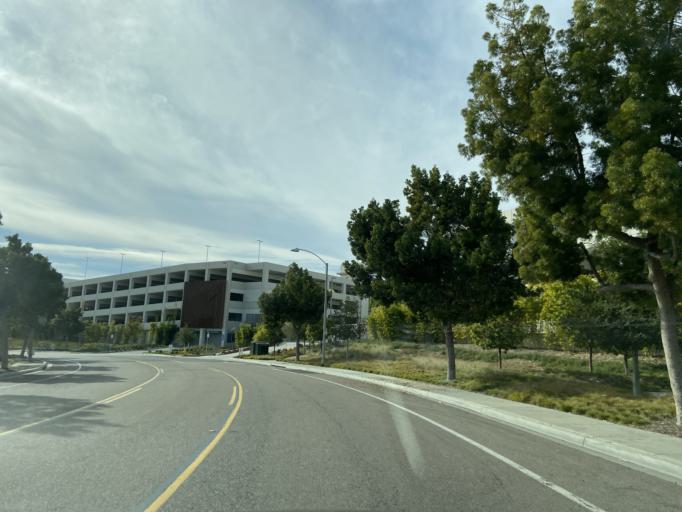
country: US
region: California
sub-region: San Diego County
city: Lake San Marcos
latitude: 33.1256
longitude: -117.2637
